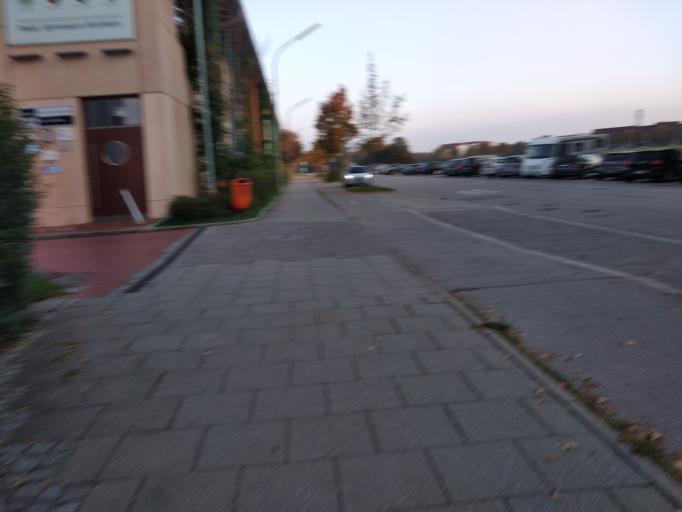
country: DE
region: Bavaria
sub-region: Upper Bavaria
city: Kirchheim bei Muenchen
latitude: 48.1678
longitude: 11.7583
